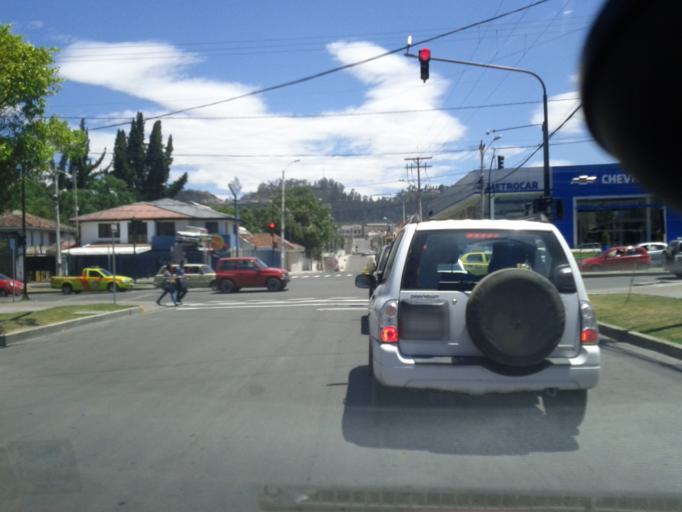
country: EC
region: Azuay
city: Cuenca
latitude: -2.9061
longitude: -79.0092
